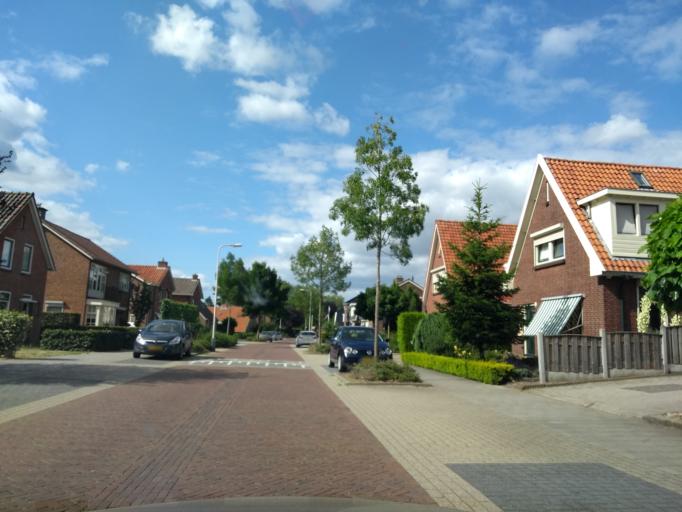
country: NL
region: Overijssel
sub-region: Gemeente Hof van Twente
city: Markelo
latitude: 52.3020
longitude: 6.5036
